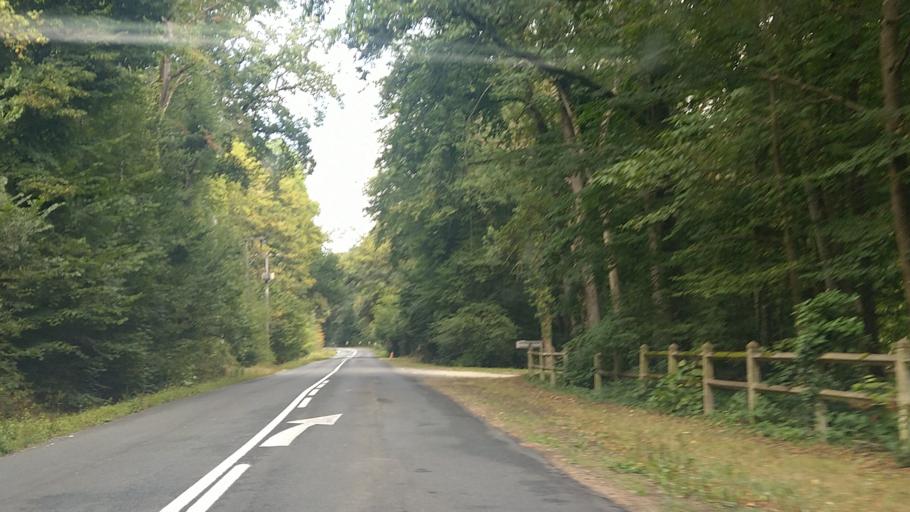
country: FR
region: Ile-de-France
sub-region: Departement des Yvelines
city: Saint-Arnoult-en-Yvelines
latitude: 48.5687
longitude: 1.9159
